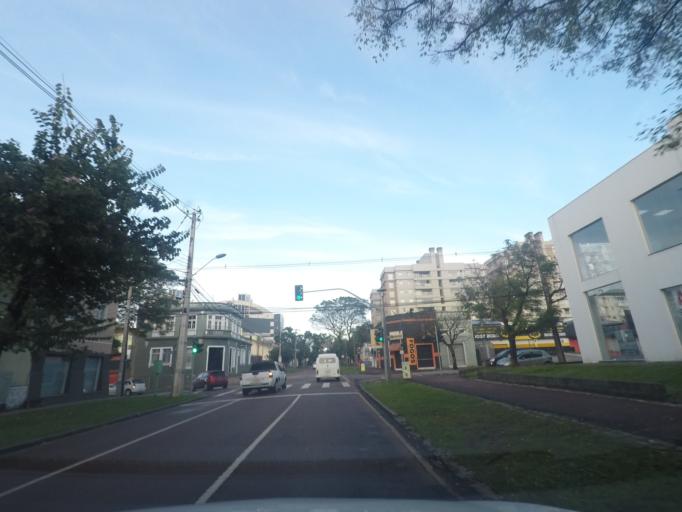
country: BR
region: Parana
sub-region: Curitiba
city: Curitiba
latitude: -25.4447
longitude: -49.2670
